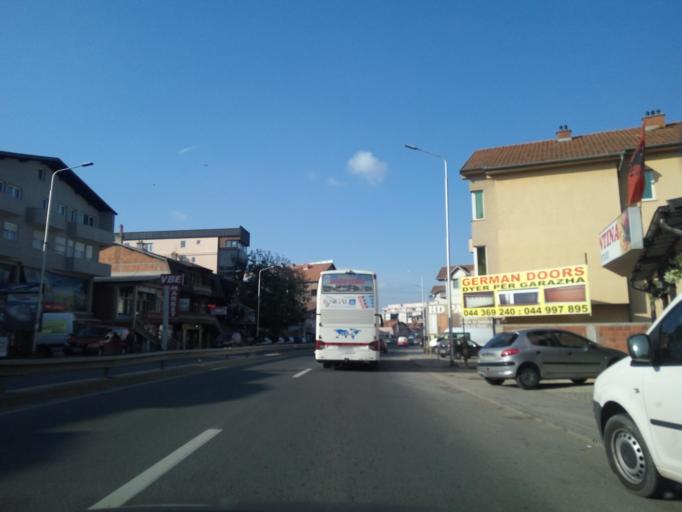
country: XK
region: Pristina
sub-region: Kosovo Polje
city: Kosovo Polje
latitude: 42.6357
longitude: 21.0919
